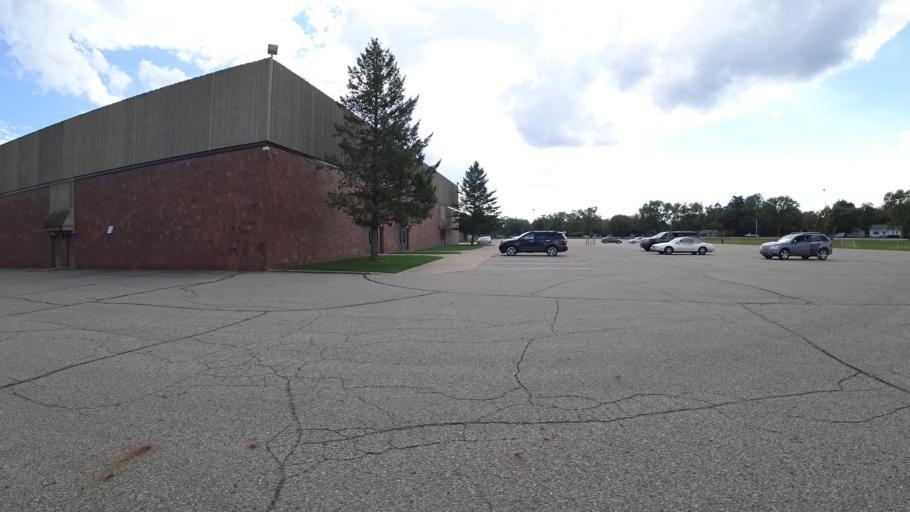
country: US
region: Michigan
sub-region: Saint Joseph County
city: Three Rivers
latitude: 41.9535
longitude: -85.6176
